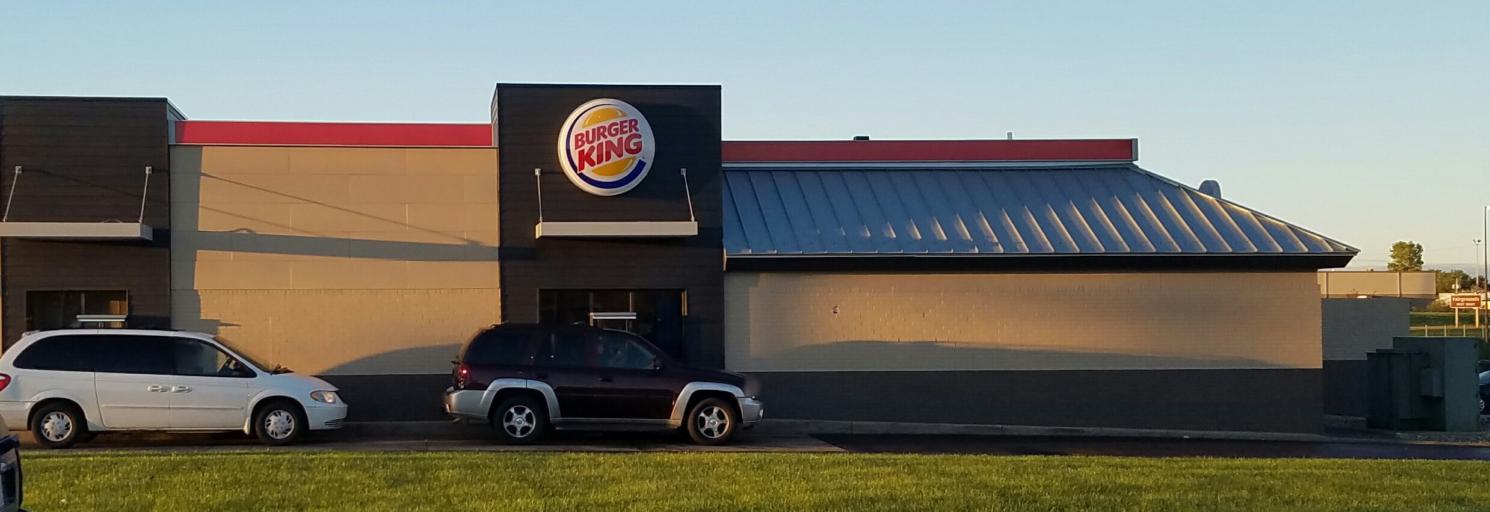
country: US
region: Ohio
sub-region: Richland County
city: Ontario
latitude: 40.7672
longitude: -82.5899
